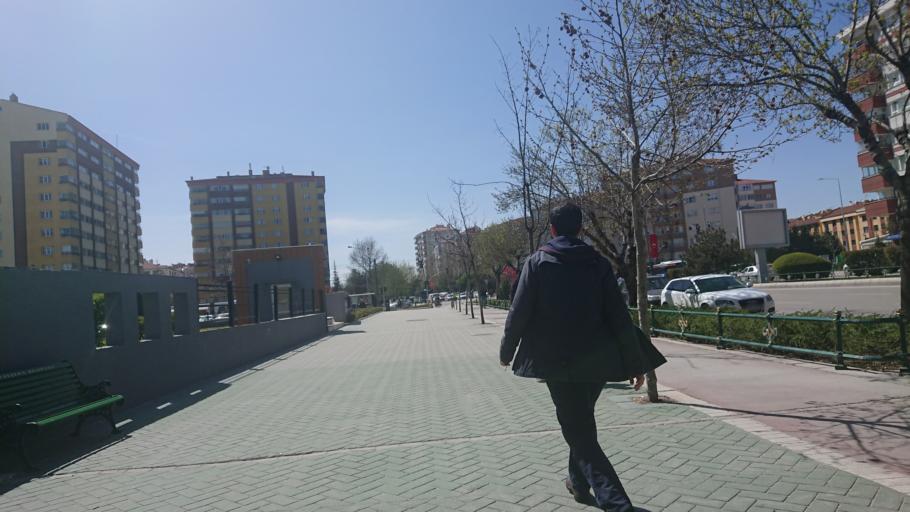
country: TR
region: Eskisehir
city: Eskisehir
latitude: 39.7646
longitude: 30.5020
